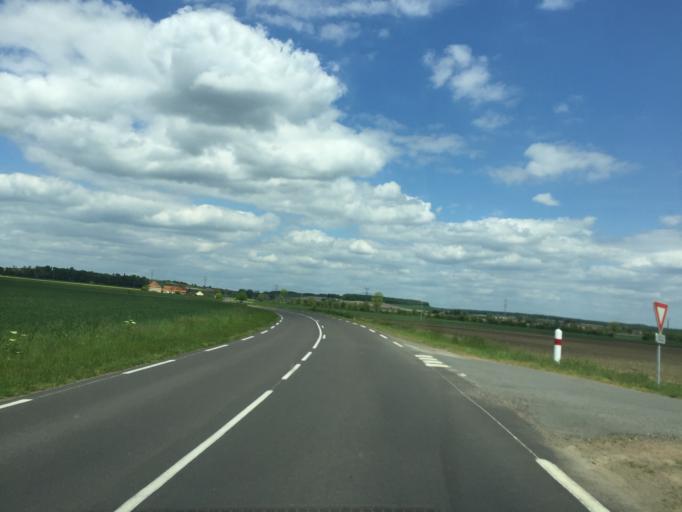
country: FR
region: Auvergne
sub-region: Departement du Puy-de-Dome
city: Aigueperse
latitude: 46.0469
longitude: 3.2631
